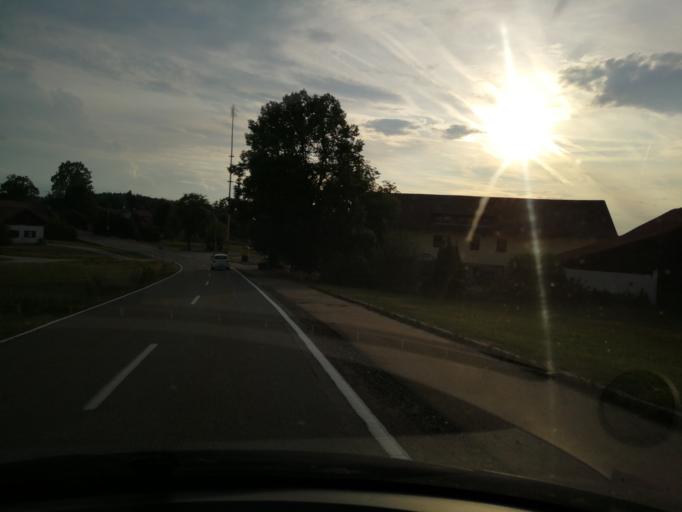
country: DE
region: Bavaria
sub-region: Lower Bavaria
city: Wiesenfelden
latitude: 49.0569
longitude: 12.5789
